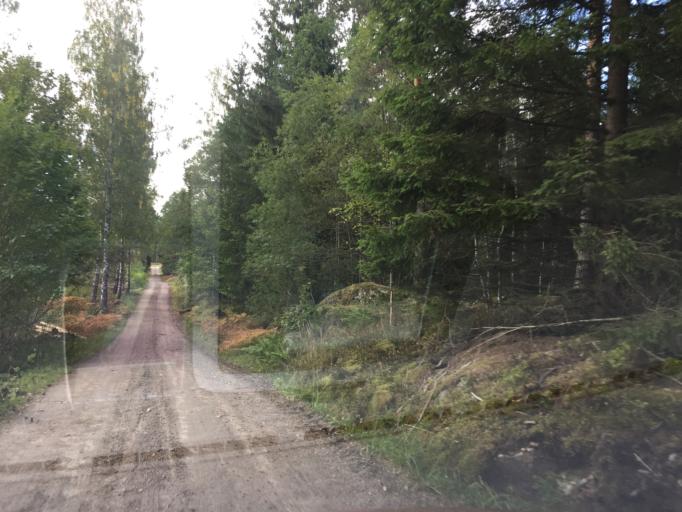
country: SE
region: Soedermanland
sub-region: Vingakers Kommun
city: Vingaker
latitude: 58.9906
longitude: 15.6888
